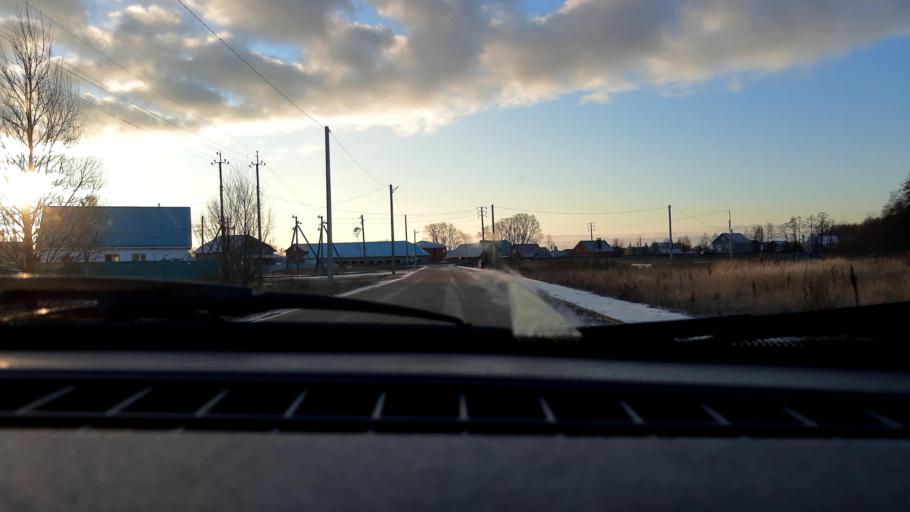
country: RU
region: Bashkortostan
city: Mikhaylovka
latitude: 54.7827
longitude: 55.8206
